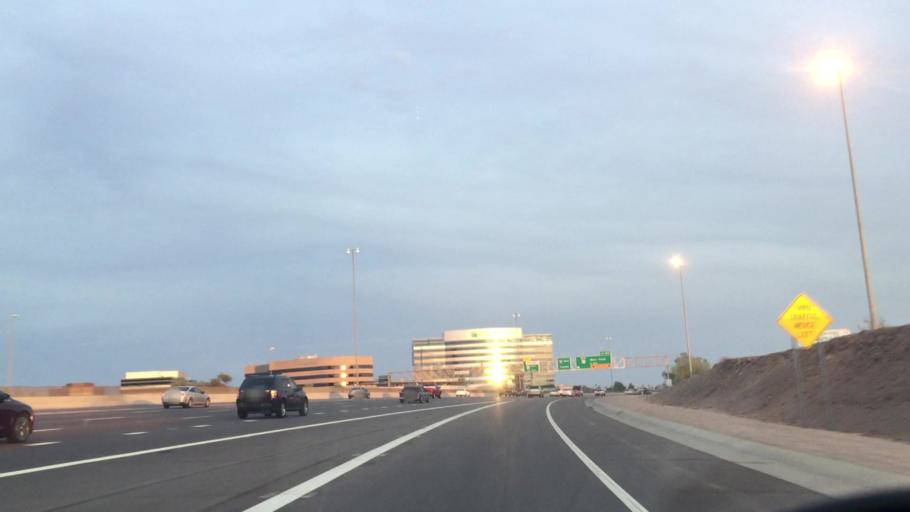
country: US
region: Arizona
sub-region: Maricopa County
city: Tempe Junction
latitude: 33.4061
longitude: -111.9698
